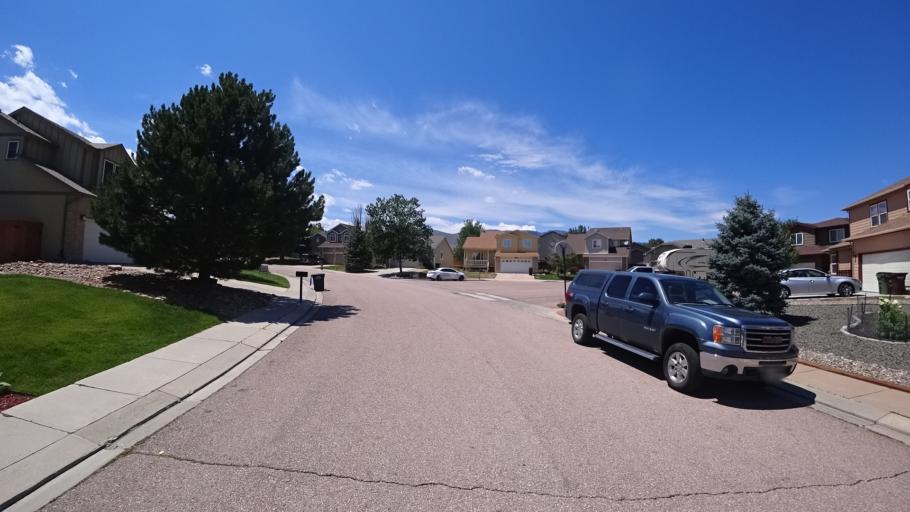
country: US
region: Colorado
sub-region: El Paso County
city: Air Force Academy
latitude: 38.9200
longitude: -104.8358
